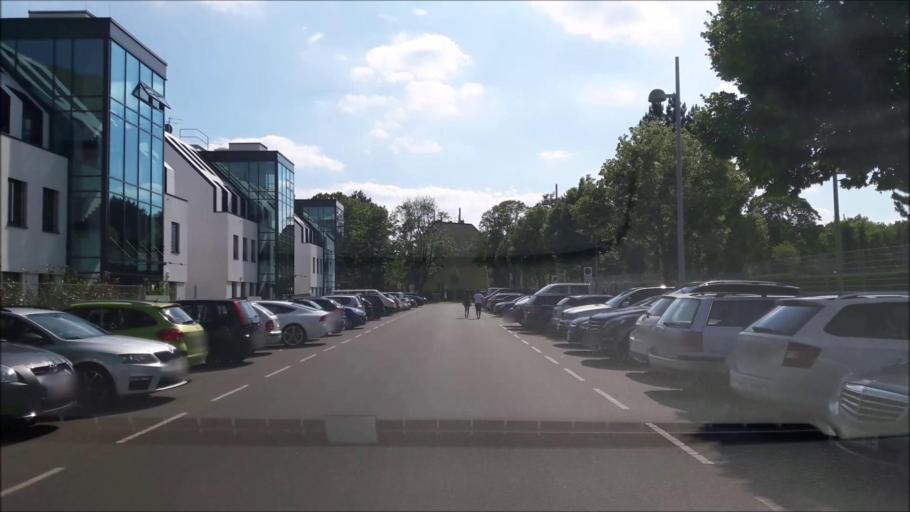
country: AT
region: Lower Austria
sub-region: Politischer Bezirk Modling
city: Perchtoldsdorf
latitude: 48.1743
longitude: 16.3011
